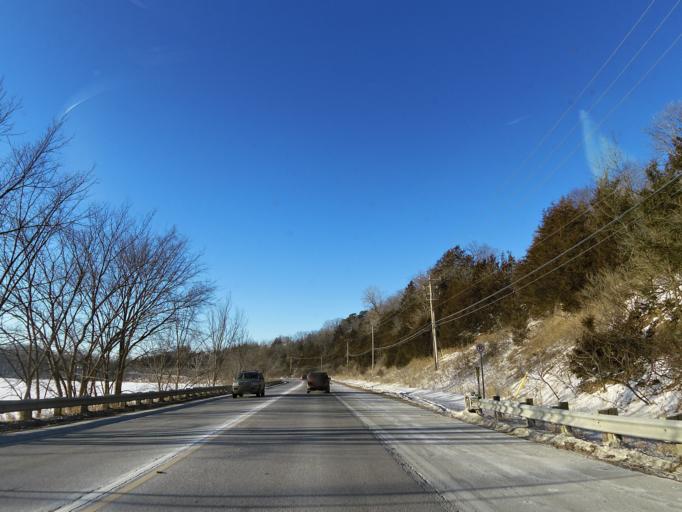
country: US
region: Minnesota
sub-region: Carver County
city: Victoria
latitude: 44.8897
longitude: -93.6594
